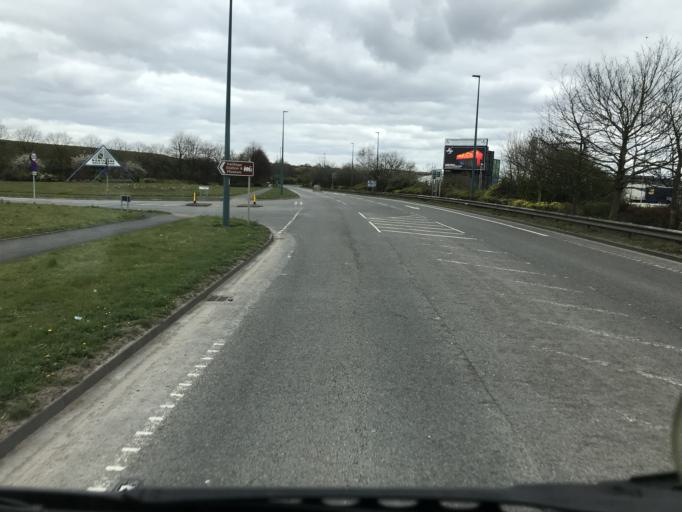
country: GB
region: England
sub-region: City and Borough of Salford
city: Irlam
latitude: 53.4329
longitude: -2.4216
